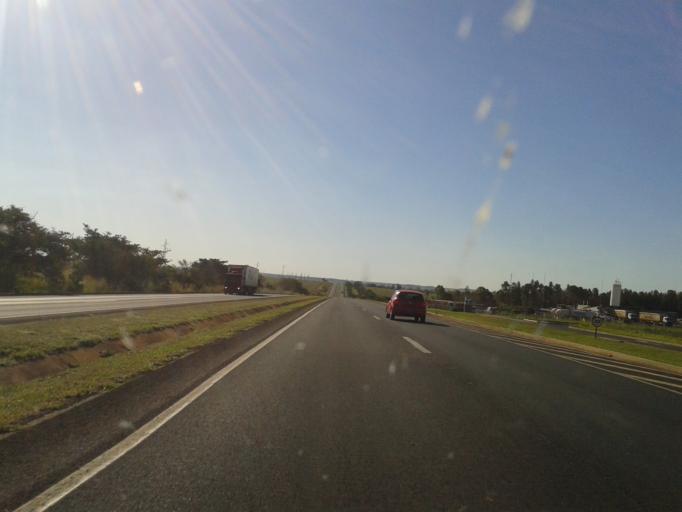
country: BR
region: Minas Gerais
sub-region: Uberlandia
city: Uberlandia
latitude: -19.0392
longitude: -48.1996
